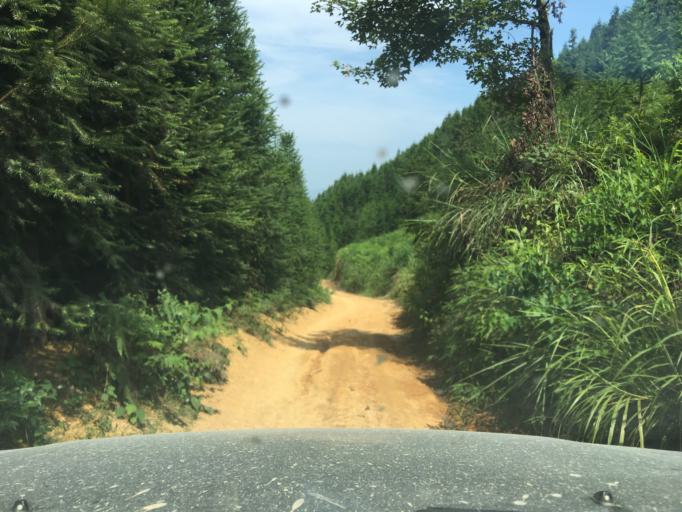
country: CN
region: Guangxi Zhuangzu Zizhiqu
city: Xinzhou
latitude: 25.0453
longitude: 105.8622
